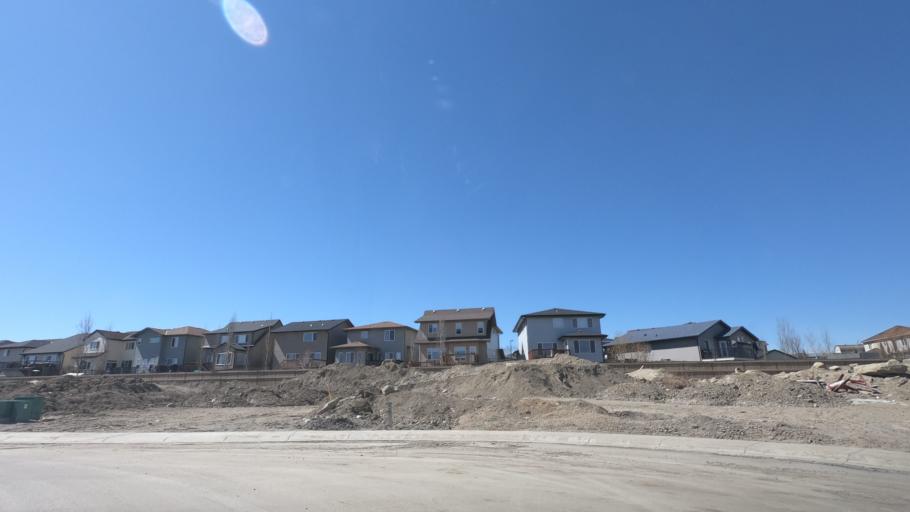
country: CA
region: Alberta
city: Airdrie
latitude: 51.3023
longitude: -114.0451
